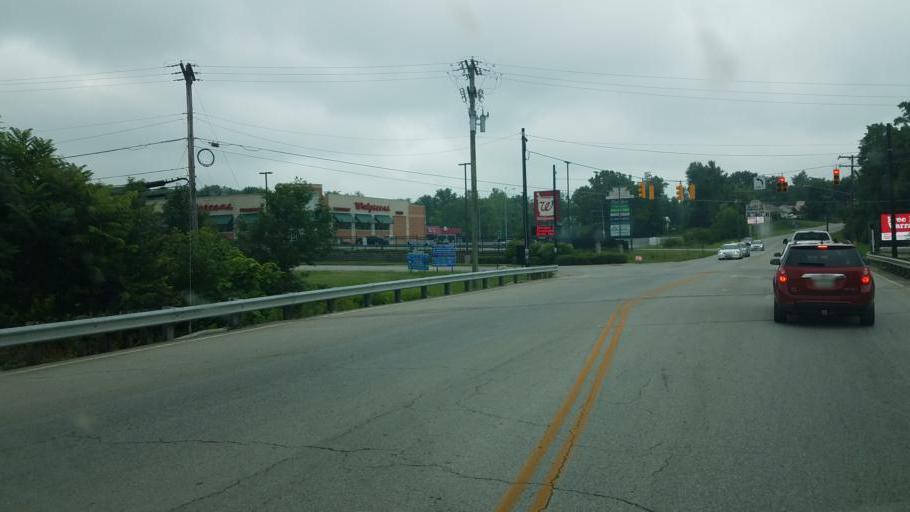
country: US
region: Ohio
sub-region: Highland County
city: Hillsboro
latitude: 39.2201
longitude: -83.6086
